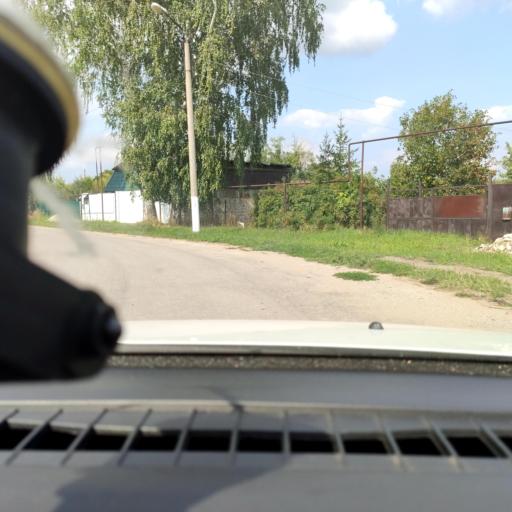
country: RU
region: Samara
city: Chapayevsk
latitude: 53.0135
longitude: 49.7499
